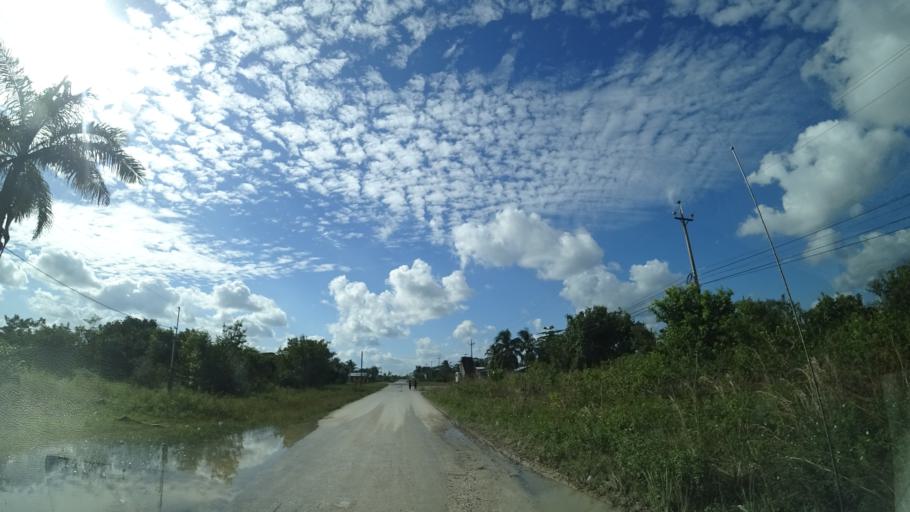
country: BZ
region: Belize
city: Belize City
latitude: 17.5693
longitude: -88.4164
